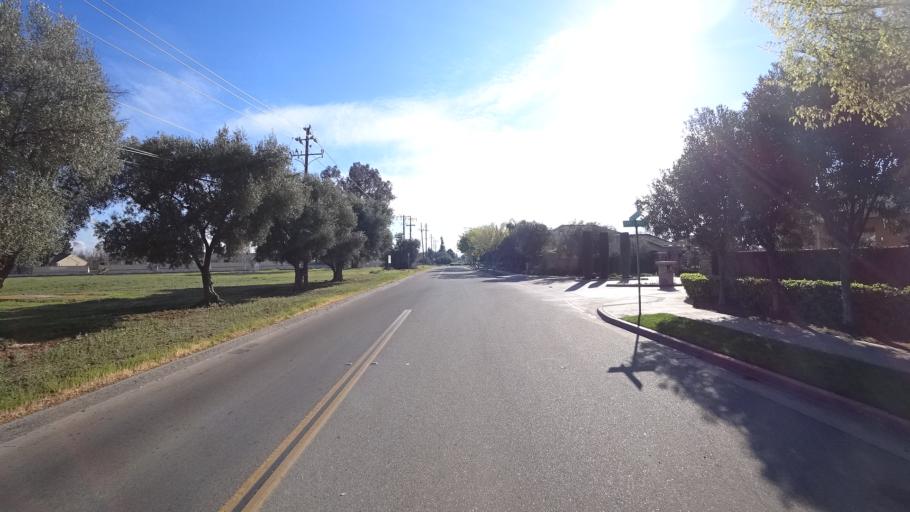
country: US
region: California
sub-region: Fresno County
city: West Park
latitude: 36.8226
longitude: -119.8655
